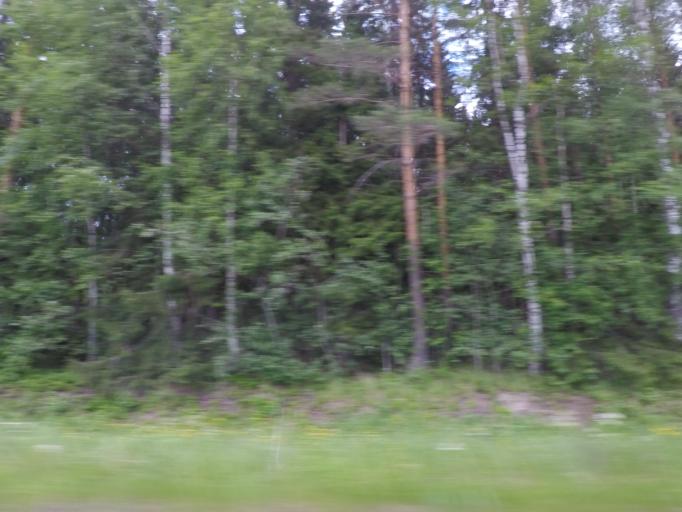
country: FI
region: Paijanne Tavastia
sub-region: Lahti
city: Hollola
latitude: 60.8451
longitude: 25.4949
